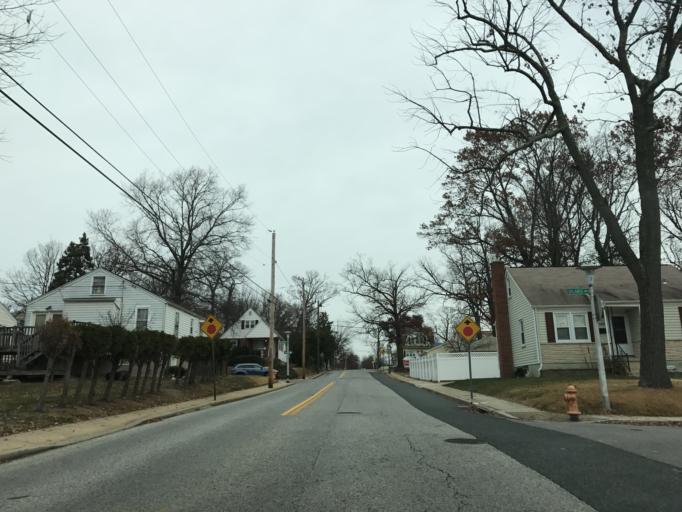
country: US
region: Maryland
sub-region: Baltimore County
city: Parkville
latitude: 39.3642
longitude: -76.5415
